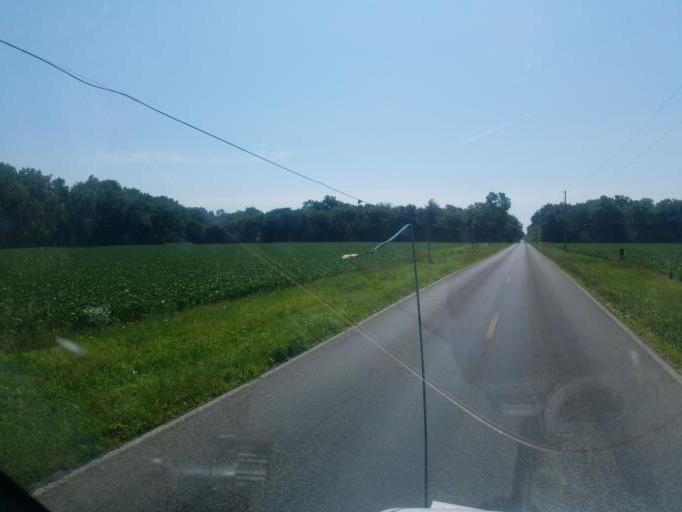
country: US
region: Ohio
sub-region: Champaign County
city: North Lewisburg
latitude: 40.2215
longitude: -83.5189
